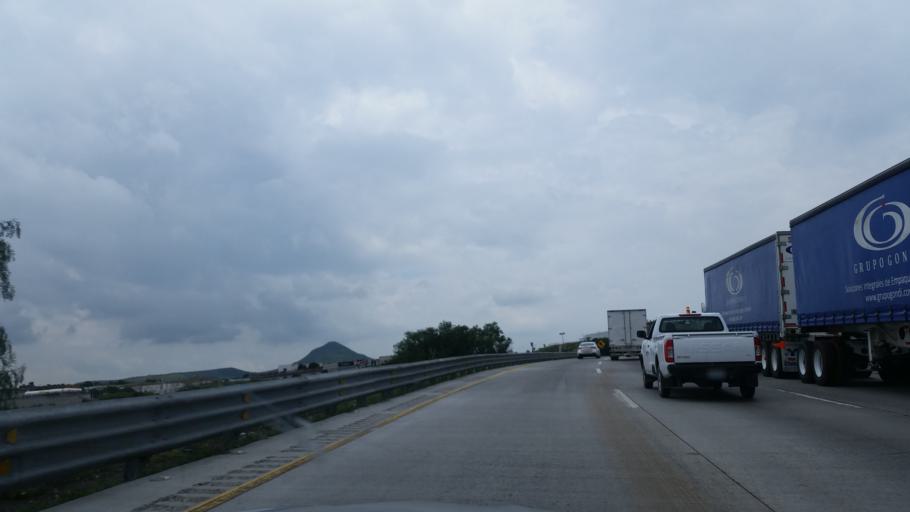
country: MX
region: Hidalgo
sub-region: Tepeji del Rio de Ocampo
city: Cantera de Villagran
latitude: 19.8574
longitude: -99.3005
